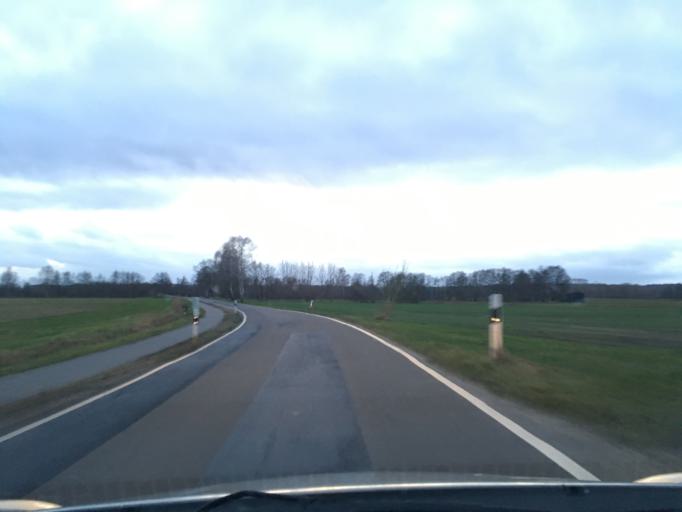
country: DE
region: Lower Saxony
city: Winsen
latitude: 53.3538
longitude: 10.1641
